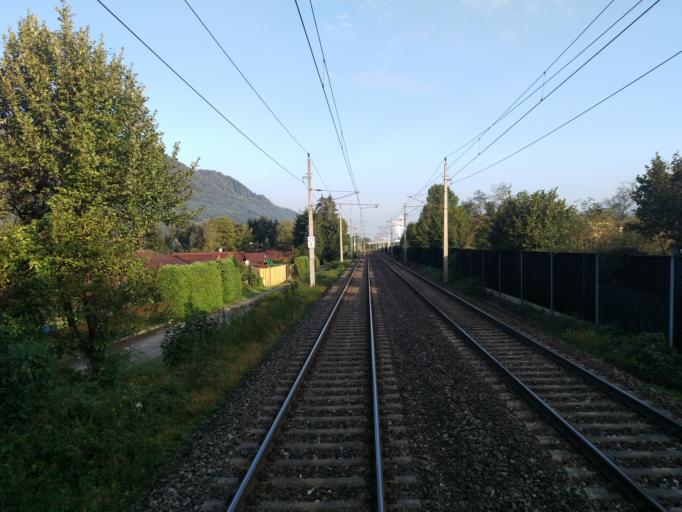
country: AT
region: Salzburg
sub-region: Politischer Bezirk Hallein
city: Kuchl
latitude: 47.6399
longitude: 13.1349
